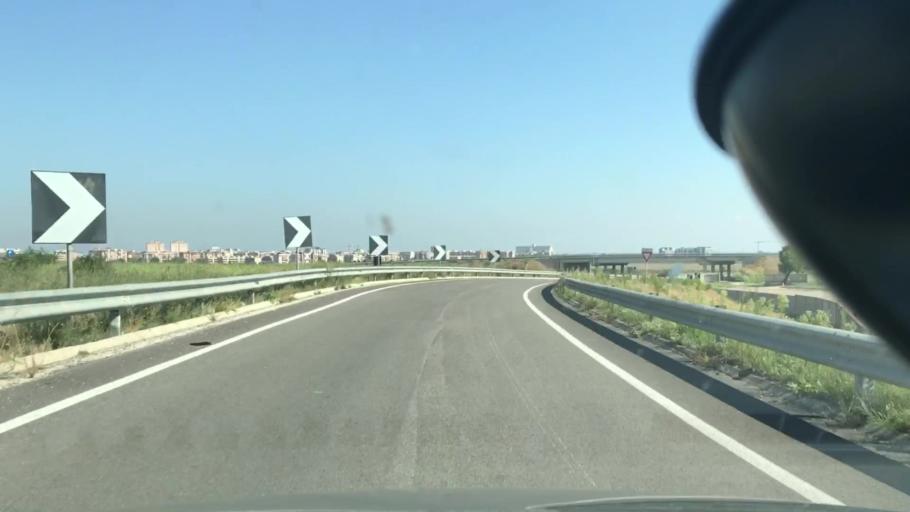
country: IT
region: Apulia
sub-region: Provincia di Foggia
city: Foggia
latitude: 41.4241
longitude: 15.5595
